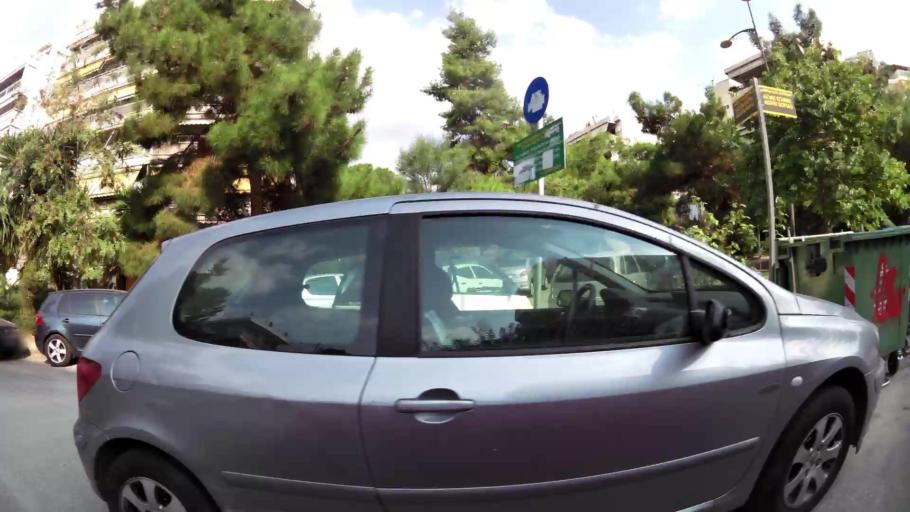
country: GR
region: Attica
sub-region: Nomarchia Athinas
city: Nea Smyrni
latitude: 37.9459
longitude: 23.7169
